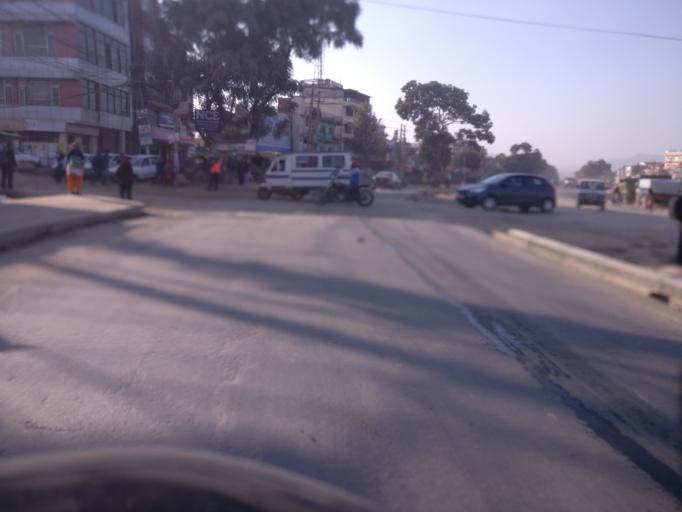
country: NP
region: Central Region
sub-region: Bagmati Zone
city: Patan
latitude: 27.6578
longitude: 85.3227
